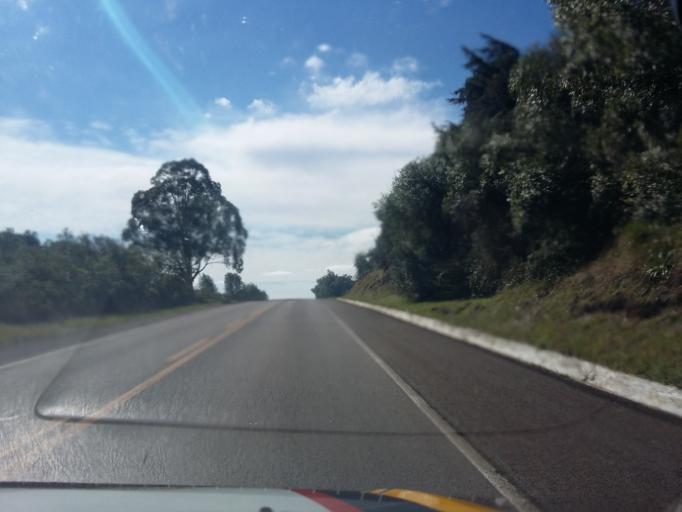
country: BR
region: Rio Grande do Sul
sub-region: Vacaria
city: Vacaria
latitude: -28.6420
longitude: -51.0449
